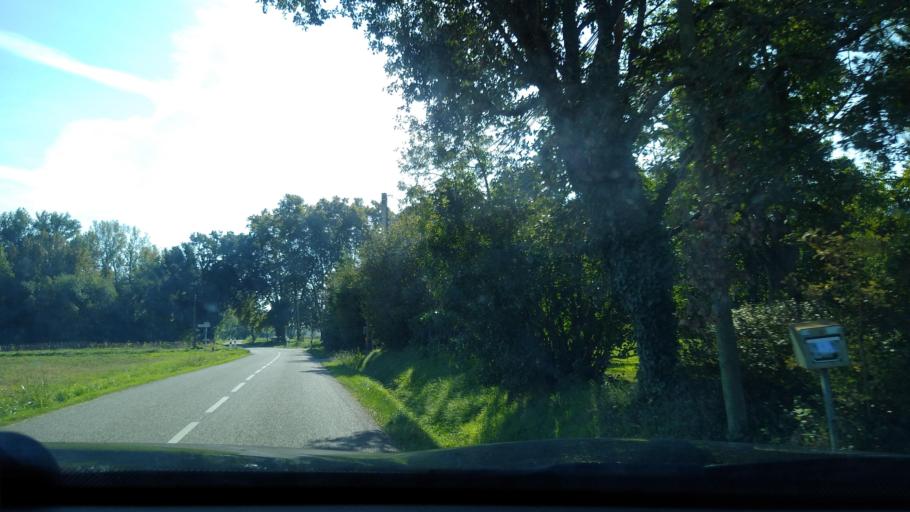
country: FR
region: Midi-Pyrenees
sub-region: Departement de la Haute-Garonne
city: Montaigut-sur-Save
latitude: 43.7297
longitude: 1.2382
